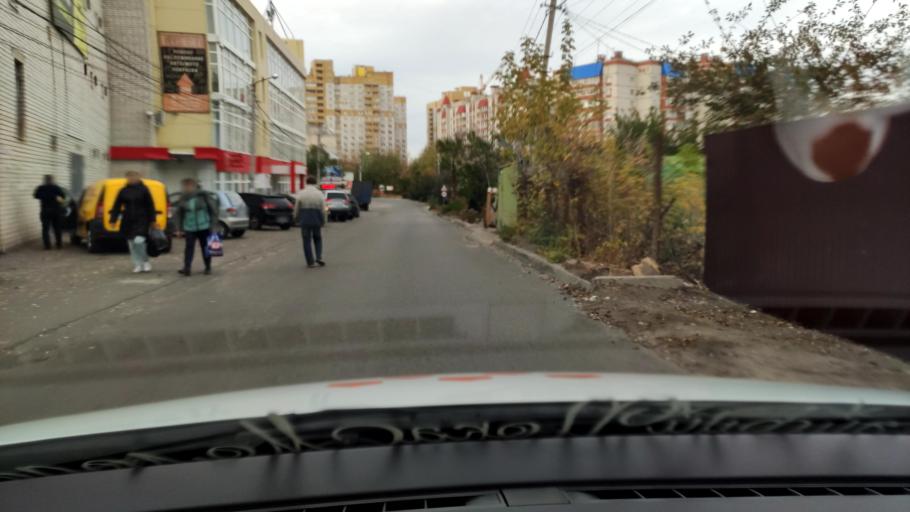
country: RU
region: Voronezj
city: Voronezh
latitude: 51.6980
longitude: 39.2051
